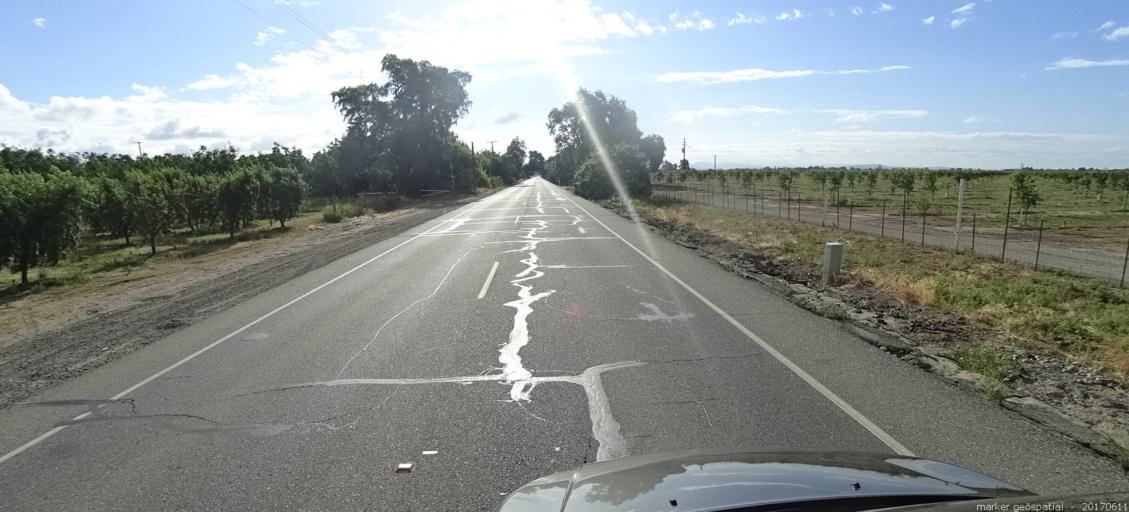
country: US
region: California
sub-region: Butte County
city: Gridley
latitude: 39.3643
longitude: -121.6275
